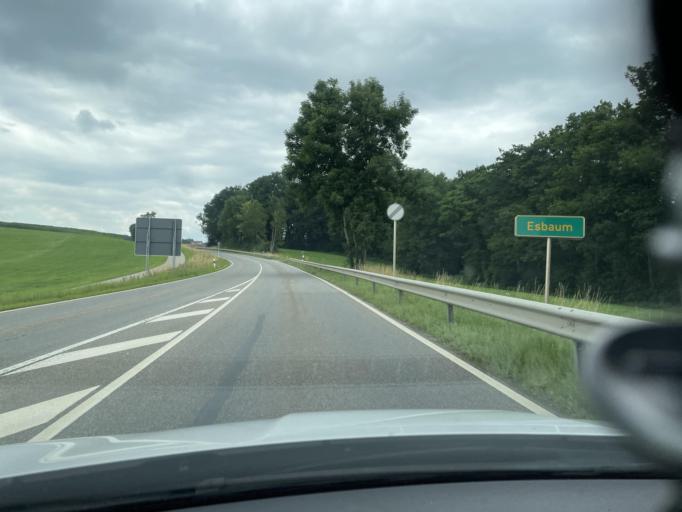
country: DE
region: Bavaria
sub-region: Upper Bavaria
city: Haag in Oberbayern
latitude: 48.1712
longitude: 12.1621
